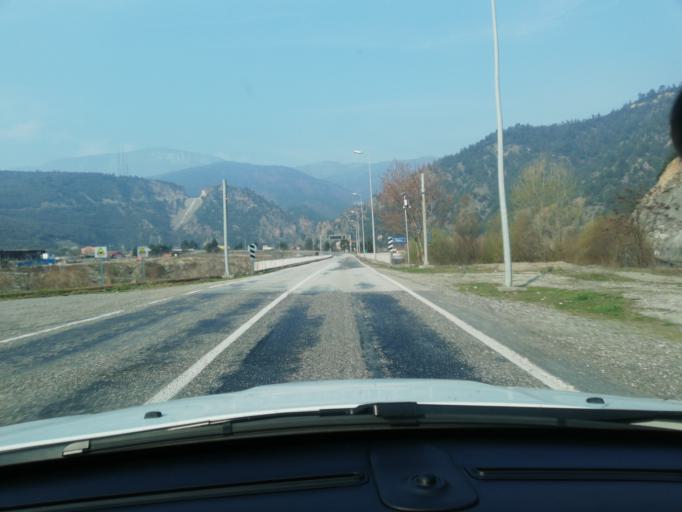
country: TR
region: Karabuk
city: Karabuk
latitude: 41.1558
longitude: 32.5400
